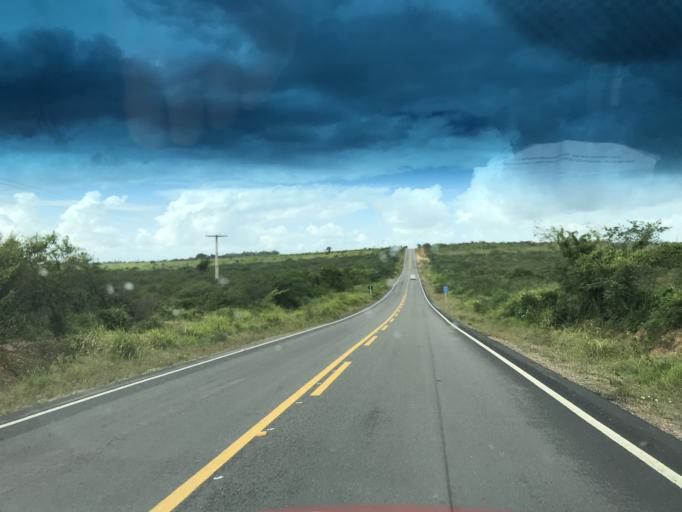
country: BR
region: Bahia
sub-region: Conceicao Do Almeida
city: Conceicao do Almeida
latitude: -12.6735
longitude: -39.2687
